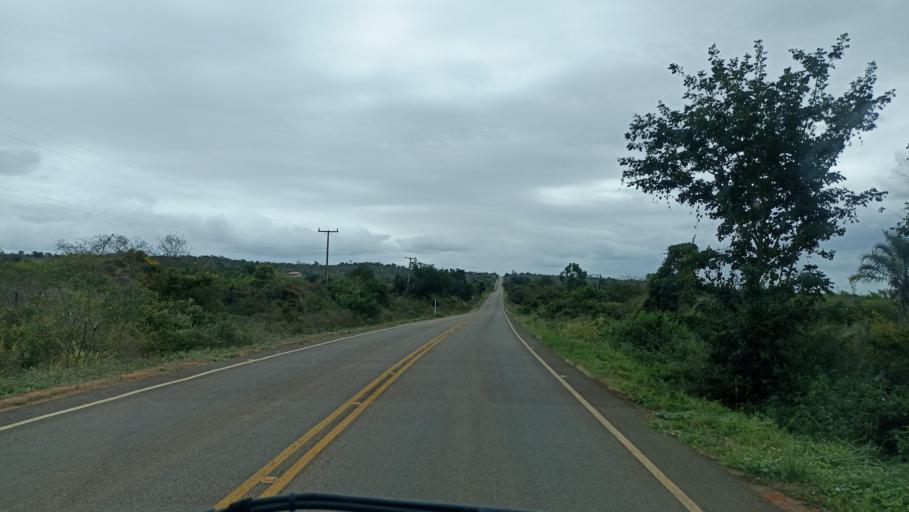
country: BR
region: Bahia
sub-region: Andarai
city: Vera Cruz
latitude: -13.0030
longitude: -40.9877
